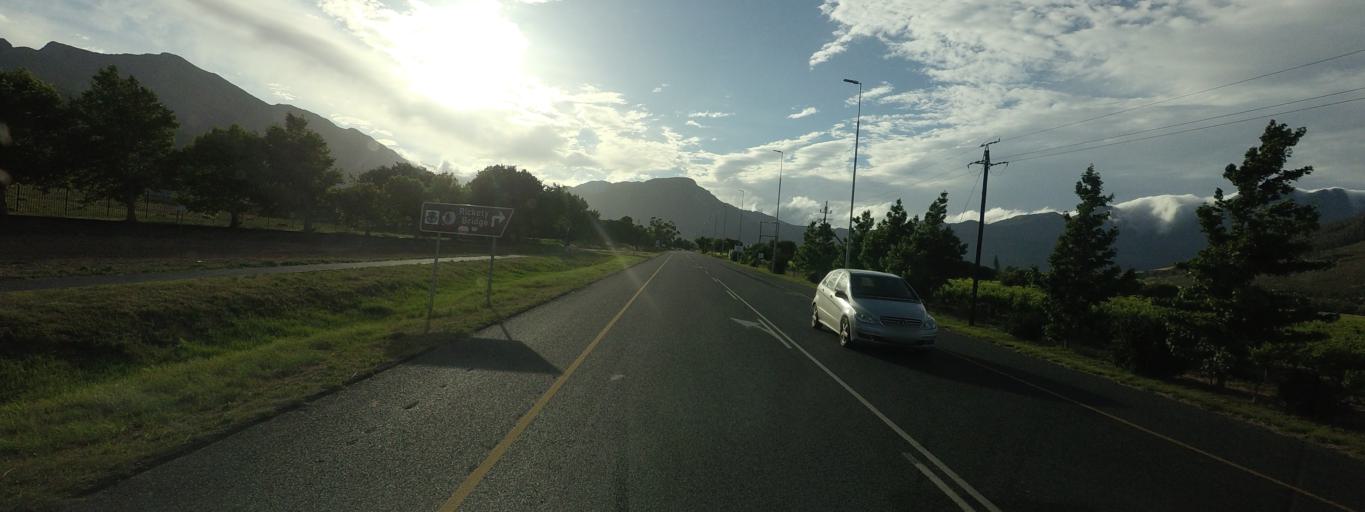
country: ZA
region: Western Cape
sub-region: Cape Winelands District Municipality
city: Paarl
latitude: -33.8934
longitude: 19.0953
